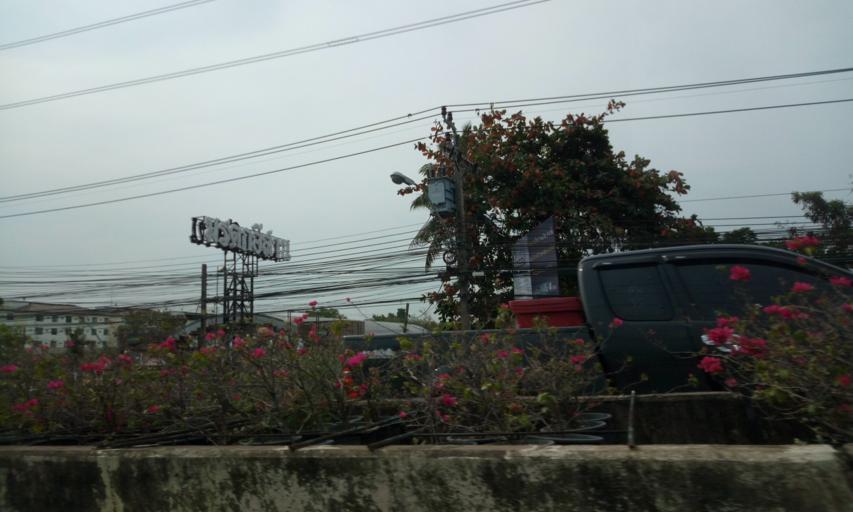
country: TH
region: Bangkok
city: Lat Krabang
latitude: 13.7217
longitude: 100.7663
